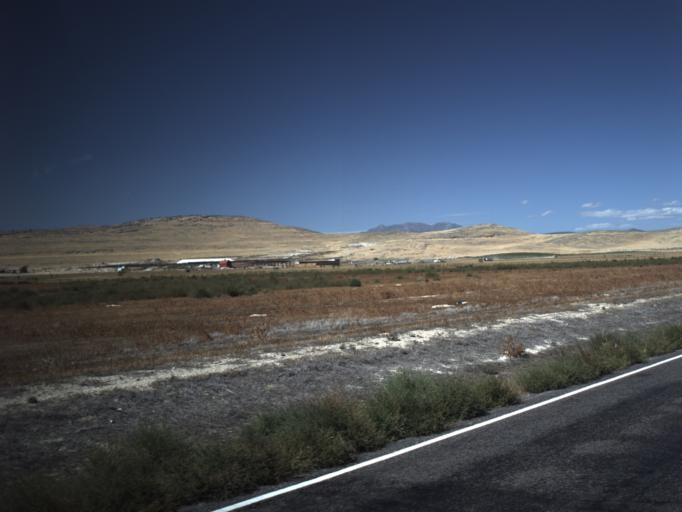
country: US
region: Utah
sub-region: Utah County
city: Genola
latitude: 40.1039
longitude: -111.9591
